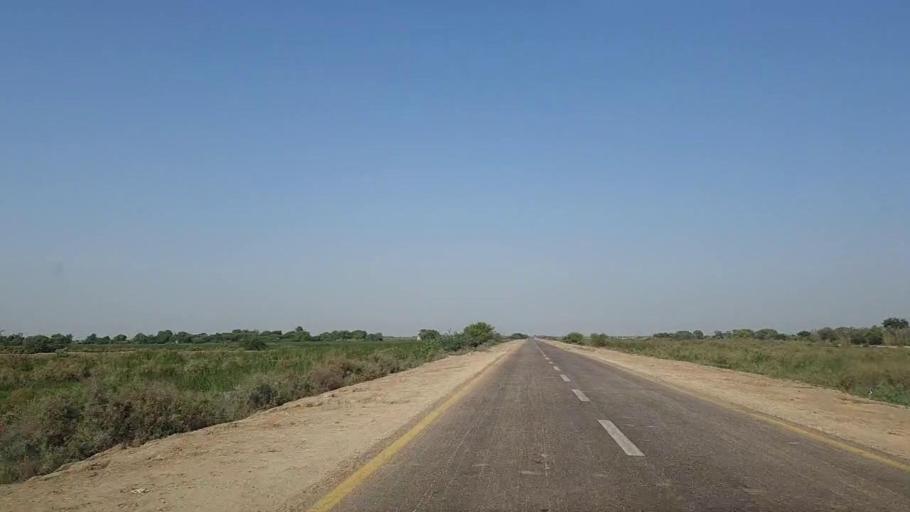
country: PK
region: Sindh
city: Jati
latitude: 24.3916
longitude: 68.2880
